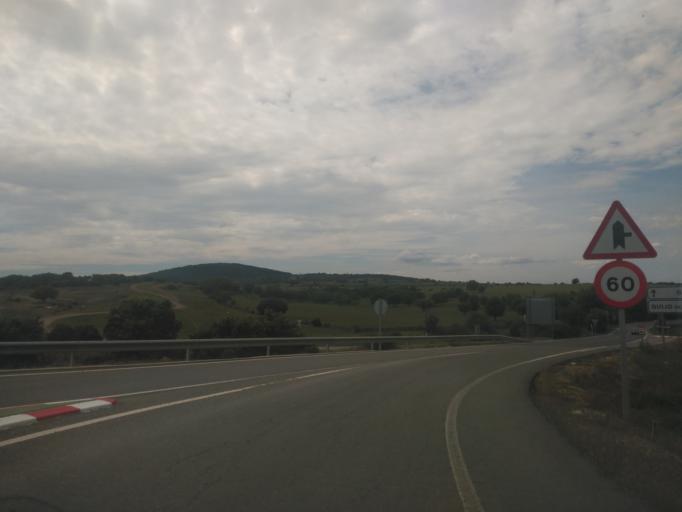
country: ES
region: Castille and Leon
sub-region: Provincia de Salamanca
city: Fuentes de Bejar
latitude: 40.5242
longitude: -5.6730
